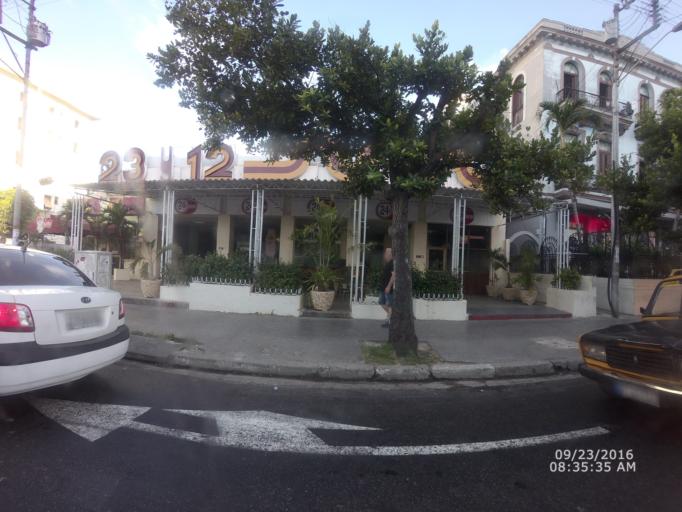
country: CU
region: La Habana
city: Havana
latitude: 23.1273
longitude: -82.3995
